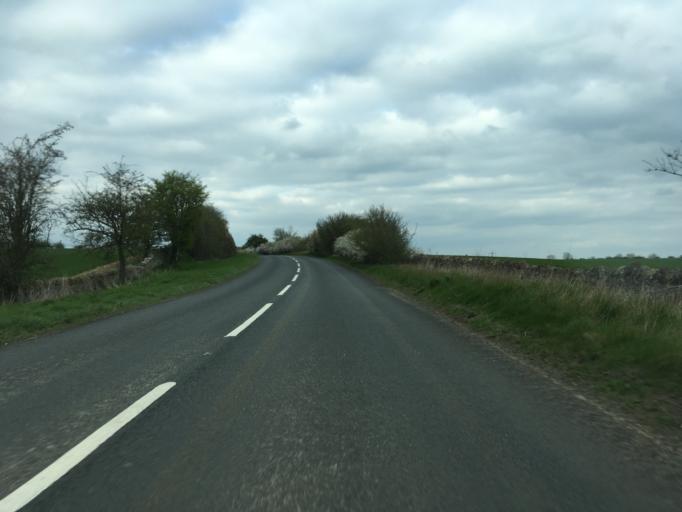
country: GB
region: England
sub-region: Gloucestershire
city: Northleach
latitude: 51.7808
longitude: -1.7878
